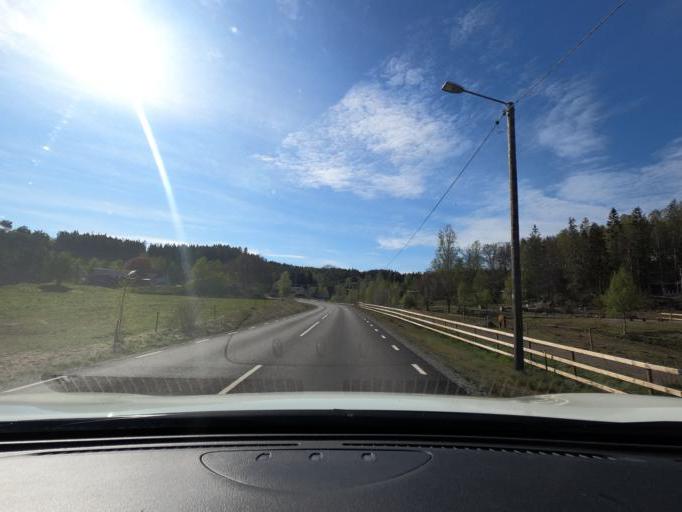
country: SE
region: Vaestra Goetaland
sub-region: Harryda Kommun
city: Landvetter
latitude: 57.6163
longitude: 12.2871
